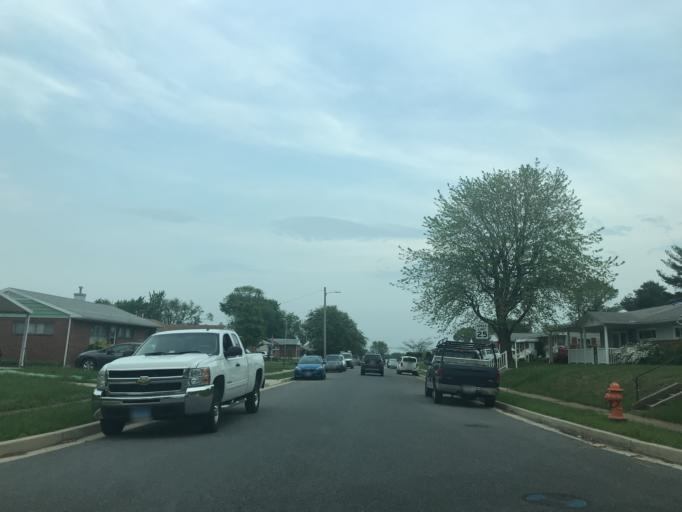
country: US
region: Maryland
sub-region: Baltimore County
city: Parkville
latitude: 39.3902
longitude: -76.5394
